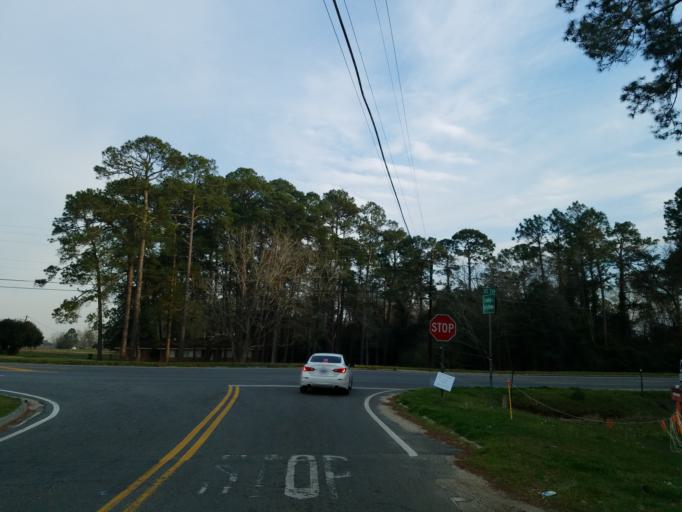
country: US
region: Georgia
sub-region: Tift County
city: Omega
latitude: 31.3435
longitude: -83.5912
